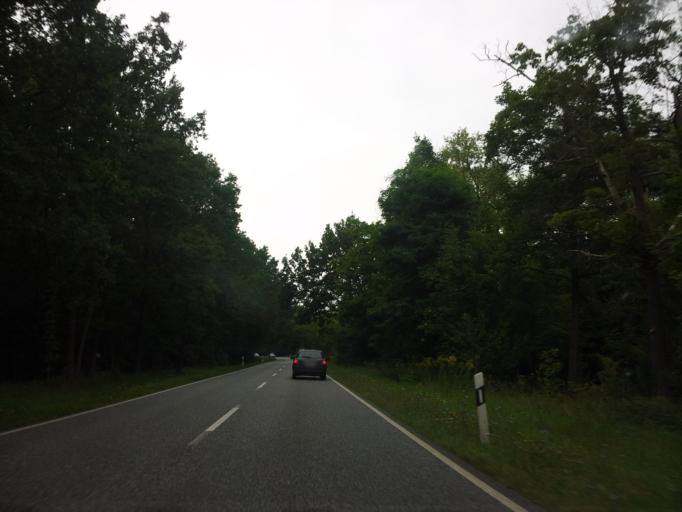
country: DE
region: Brandenburg
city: Niedergorsdorf
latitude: 52.0243
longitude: 12.9782
